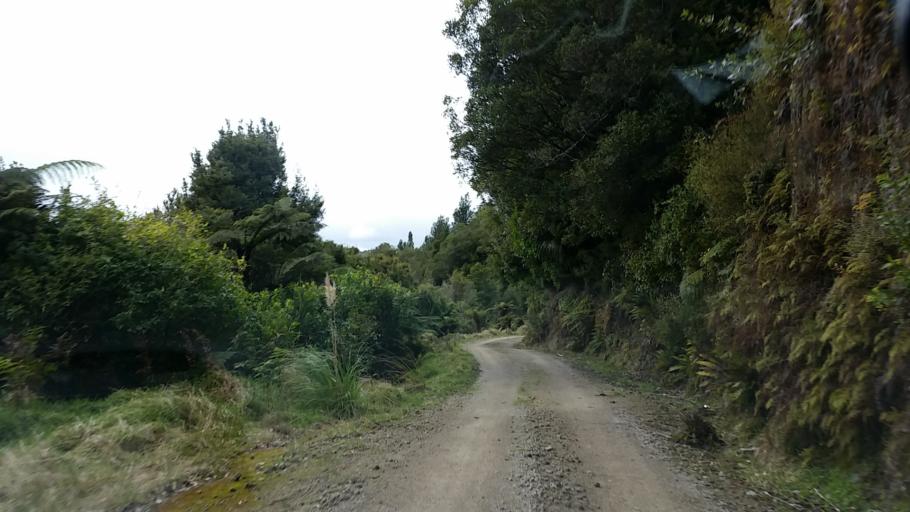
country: NZ
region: Taranaki
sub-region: South Taranaki District
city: Patea
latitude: -39.5846
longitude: 174.6842
